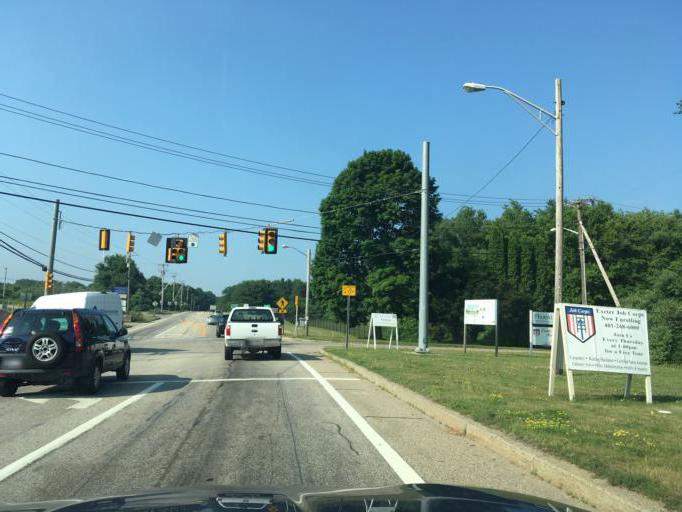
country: US
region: Rhode Island
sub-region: Washington County
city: Exeter
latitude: 41.5476
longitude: -71.5334
